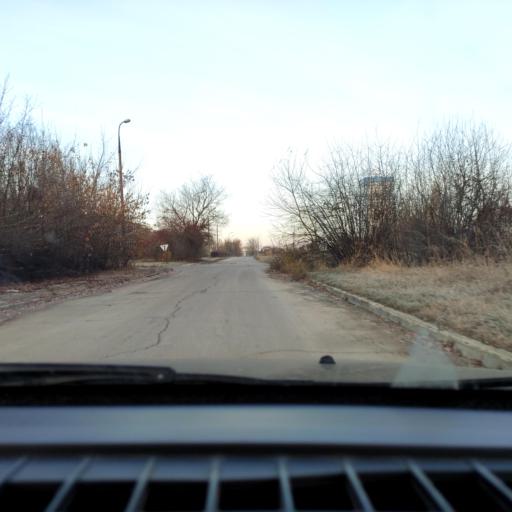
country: RU
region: Samara
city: Tol'yatti
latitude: 53.5534
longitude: 49.2746
